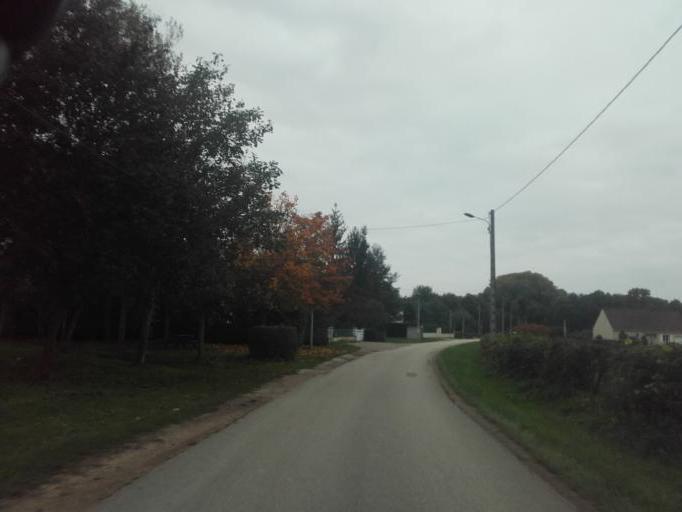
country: FR
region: Bourgogne
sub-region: Departement de Saone-et-Loire
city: Demigny
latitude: 46.9281
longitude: 4.7990
